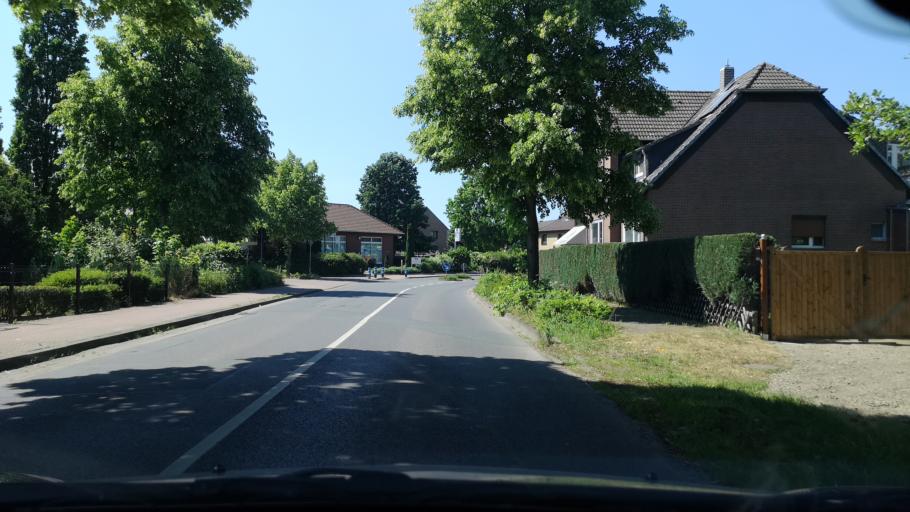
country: DE
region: Lower Saxony
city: Garbsen-Mitte
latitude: 52.4487
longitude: 9.6256
